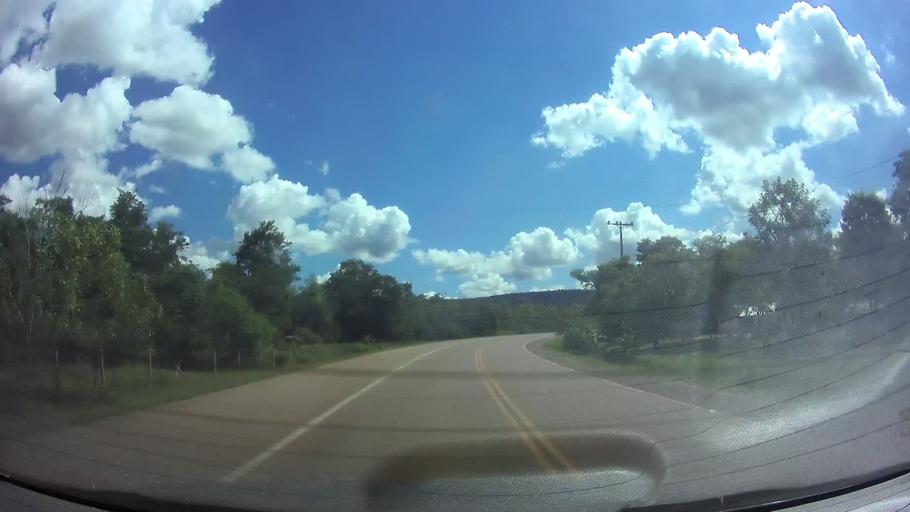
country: PY
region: Guaira
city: Itape
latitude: -25.9164
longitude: -56.7021
